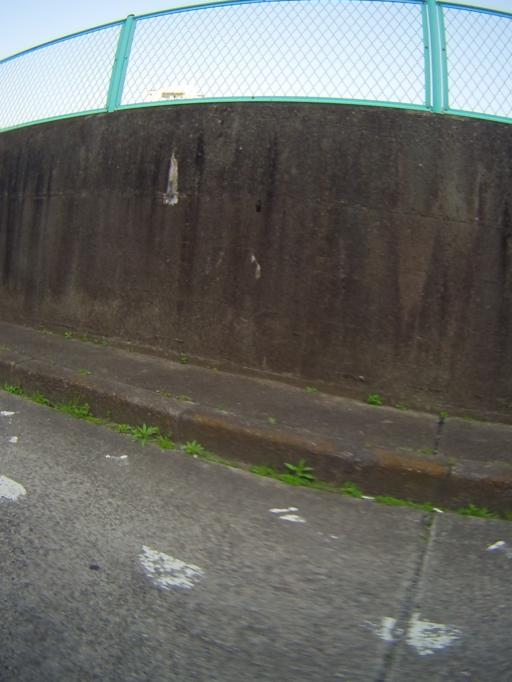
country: JP
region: Osaka
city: Osaka-shi
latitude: 34.6855
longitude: 135.4631
